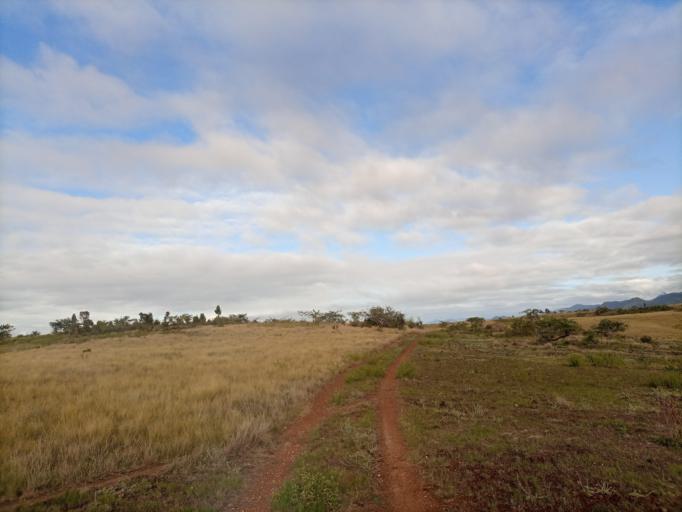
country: MG
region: Anosy
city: Fort Dauphin
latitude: -24.3146
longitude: 47.2592
